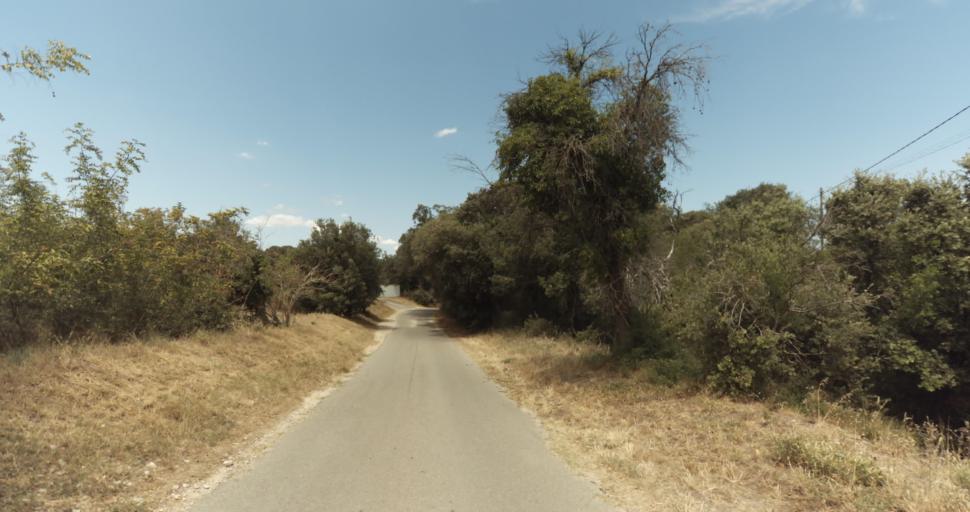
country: FR
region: Provence-Alpes-Cote d'Azur
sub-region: Departement du Vaucluse
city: Loriol-du-Comtat
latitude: 44.0568
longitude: 4.9941
